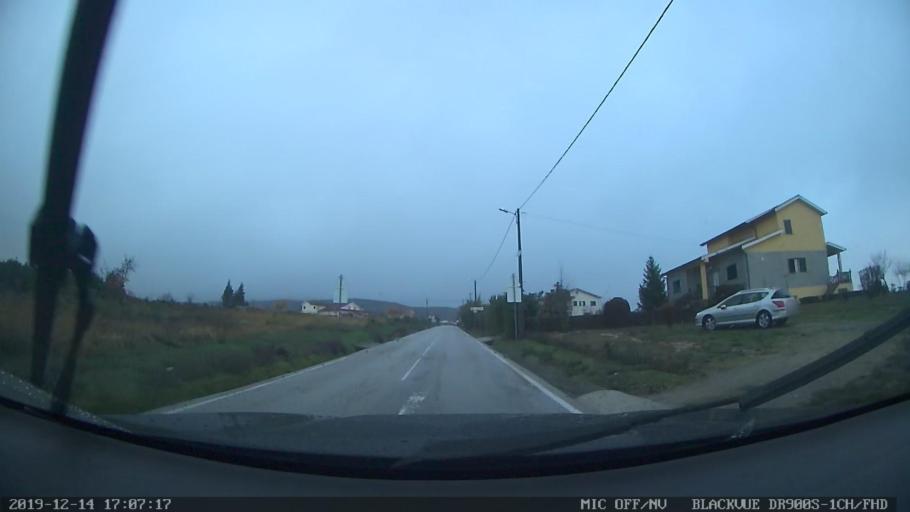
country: PT
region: Vila Real
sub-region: Vila Pouca de Aguiar
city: Vila Pouca de Aguiar
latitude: 41.4606
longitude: -7.5971
